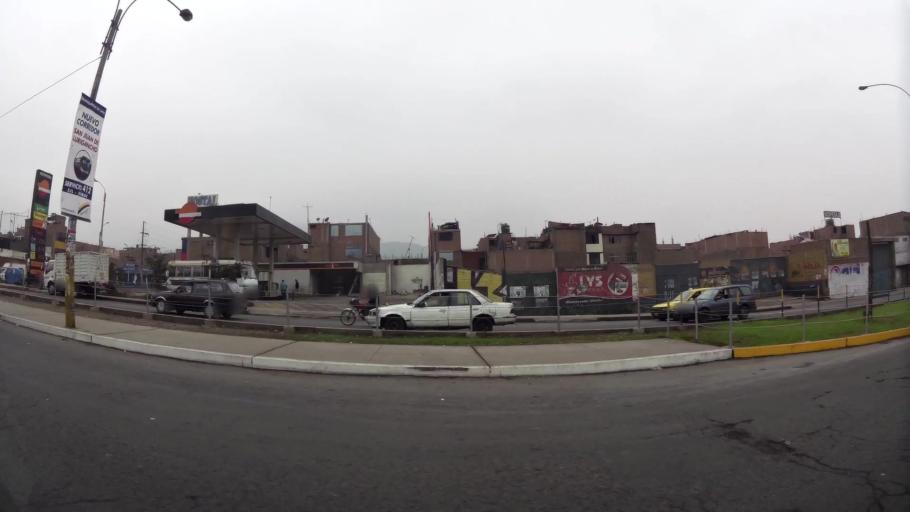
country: PE
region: Lima
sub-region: Lima
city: Independencia
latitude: -11.9439
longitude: -76.9821
